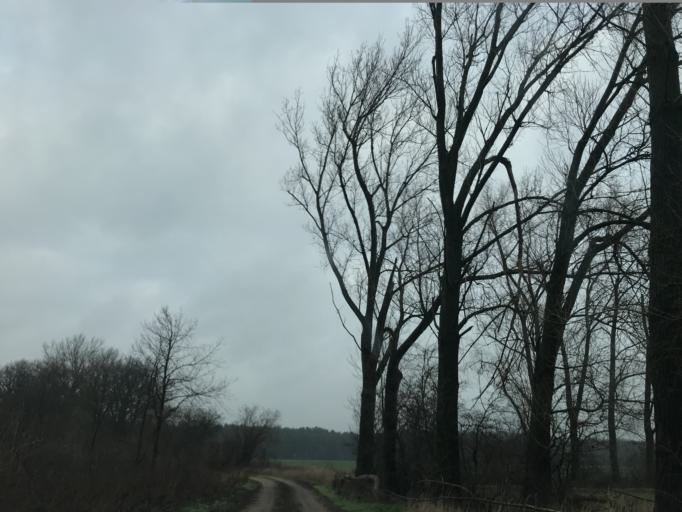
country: DE
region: Brandenburg
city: Kremmen
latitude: 52.7448
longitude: 12.9758
